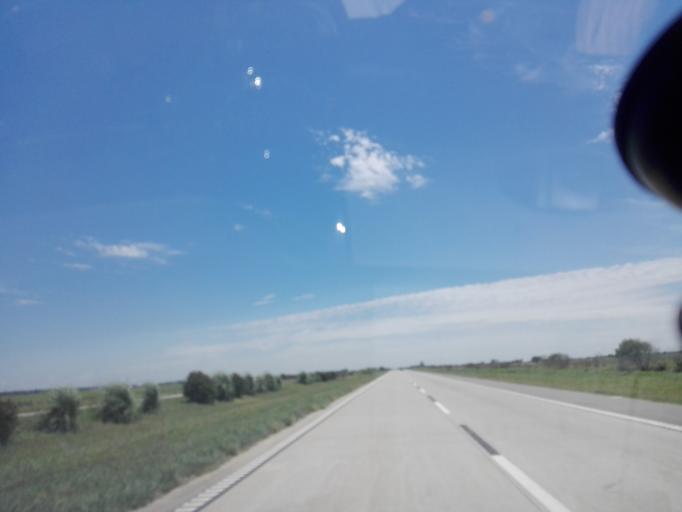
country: AR
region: Cordoba
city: Villa Maria
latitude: -32.4416
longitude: -63.1164
